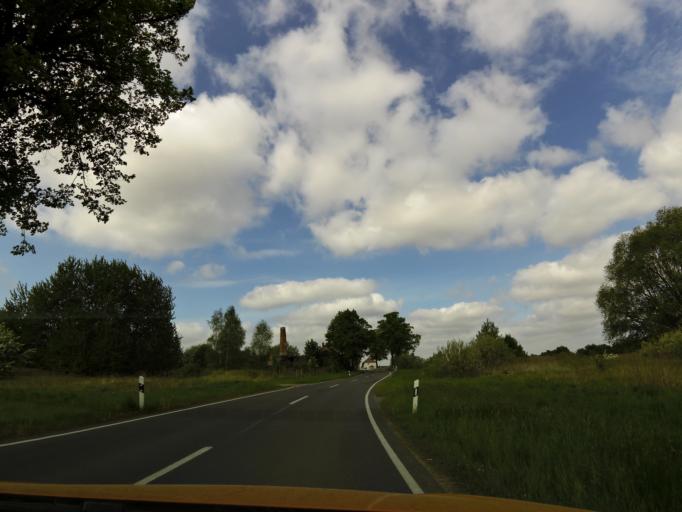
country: DE
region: Brandenburg
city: Gorzke
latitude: 52.1090
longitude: 12.3849
